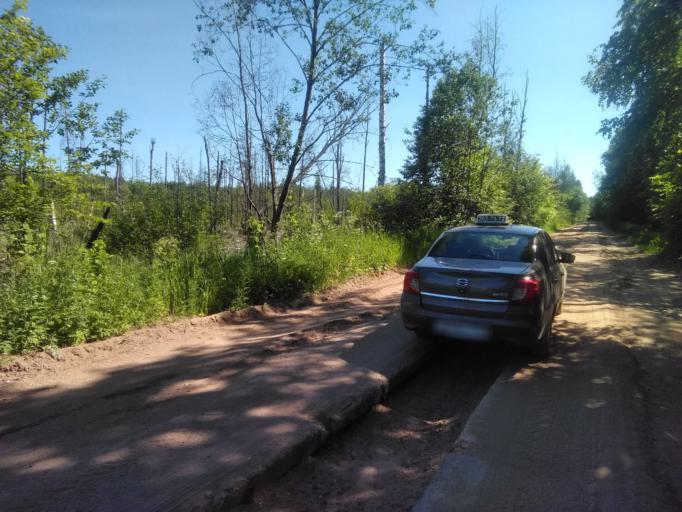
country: RU
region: Perm
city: Foki
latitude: 56.4877
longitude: 54.5572
